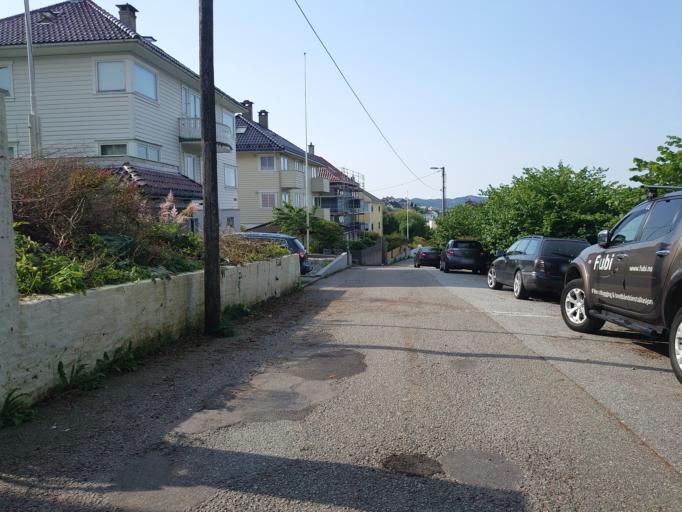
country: NO
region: Hordaland
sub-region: Bergen
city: Bergen
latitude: 60.3826
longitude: 5.3022
